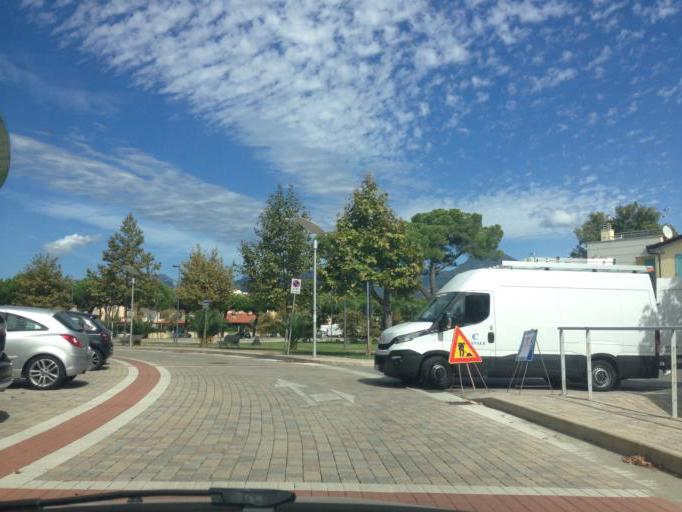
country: IT
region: Tuscany
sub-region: Provincia di Lucca
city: Camaiore
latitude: 43.8971
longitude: 10.2367
